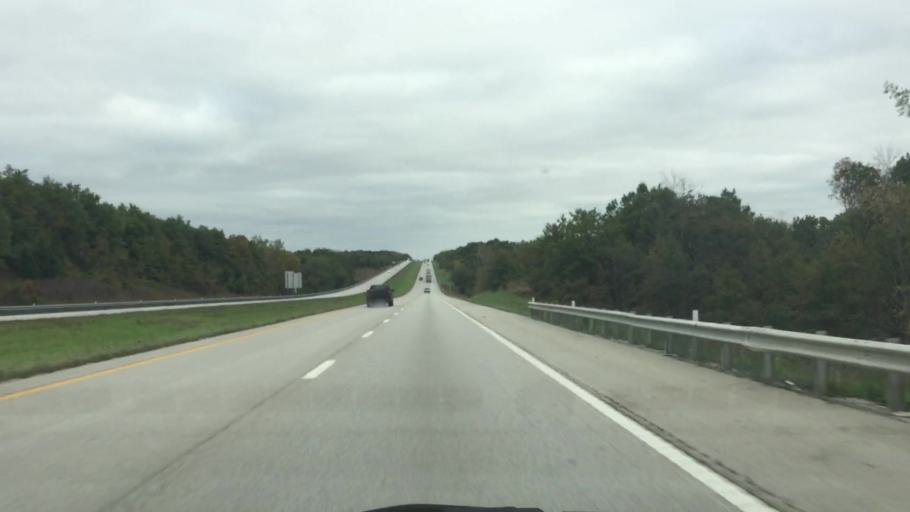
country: US
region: Missouri
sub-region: Clinton County
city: Cameron
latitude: 39.7678
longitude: -94.2144
